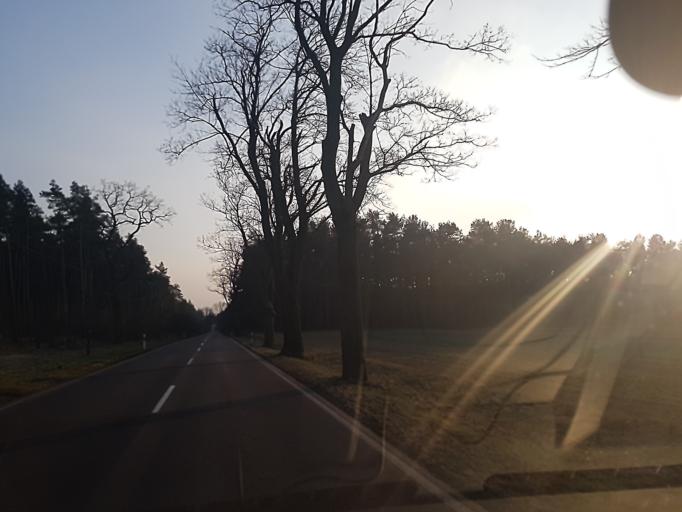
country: DE
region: Saxony-Anhalt
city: Coswig
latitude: 51.9909
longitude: 12.4712
